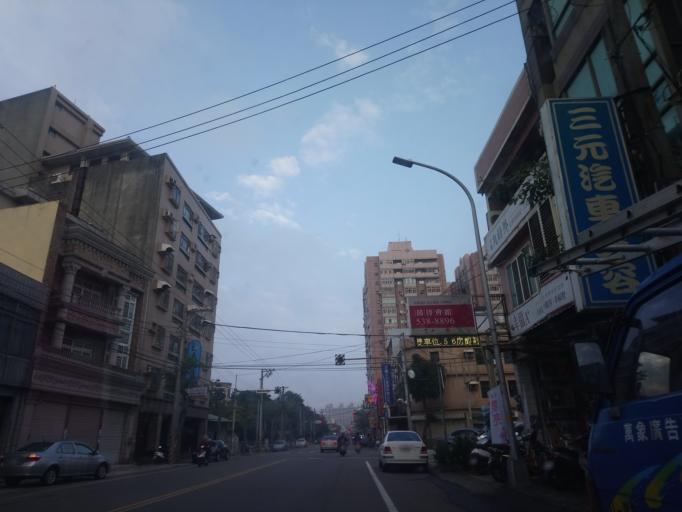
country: TW
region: Taiwan
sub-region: Hsinchu
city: Hsinchu
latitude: 24.7956
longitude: 120.9427
